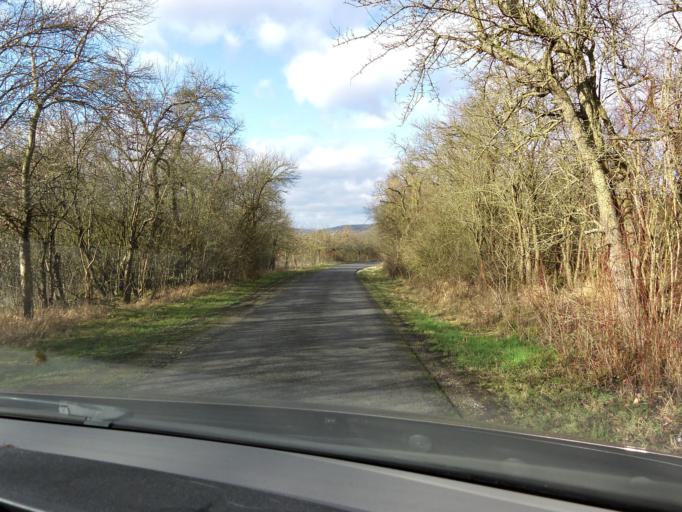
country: DE
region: Thuringia
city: Krauthausen
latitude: 51.0392
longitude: 10.2736
